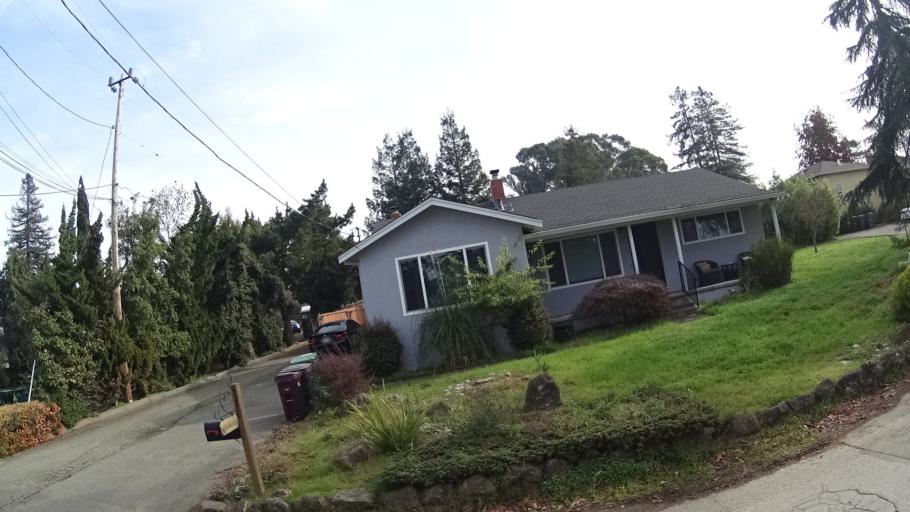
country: US
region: California
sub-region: Alameda County
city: Fairview
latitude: 37.6787
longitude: -122.0564
